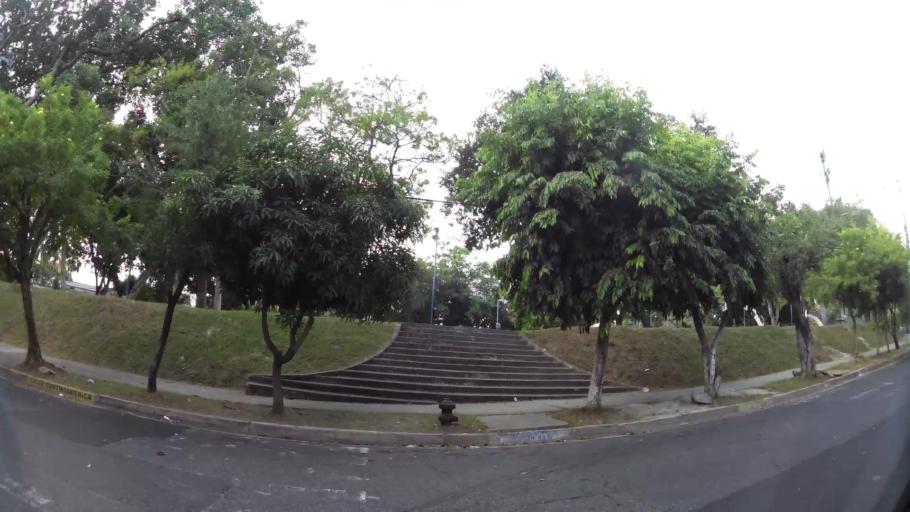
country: SV
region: San Salvador
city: Mejicanos
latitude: 13.7119
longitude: -89.2122
